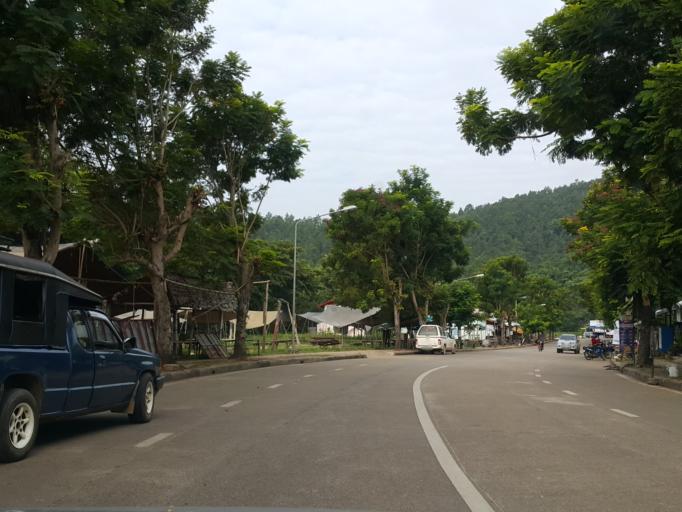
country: TH
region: Mae Hong Son
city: Mae Hong Son
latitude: 19.2928
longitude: 97.9636
